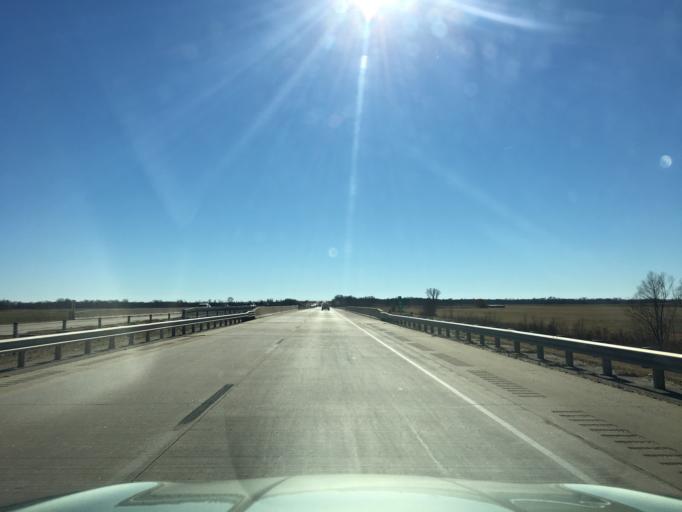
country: US
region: Oklahoma
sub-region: Noble County
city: Perry
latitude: 36.4716
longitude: -97.3272
